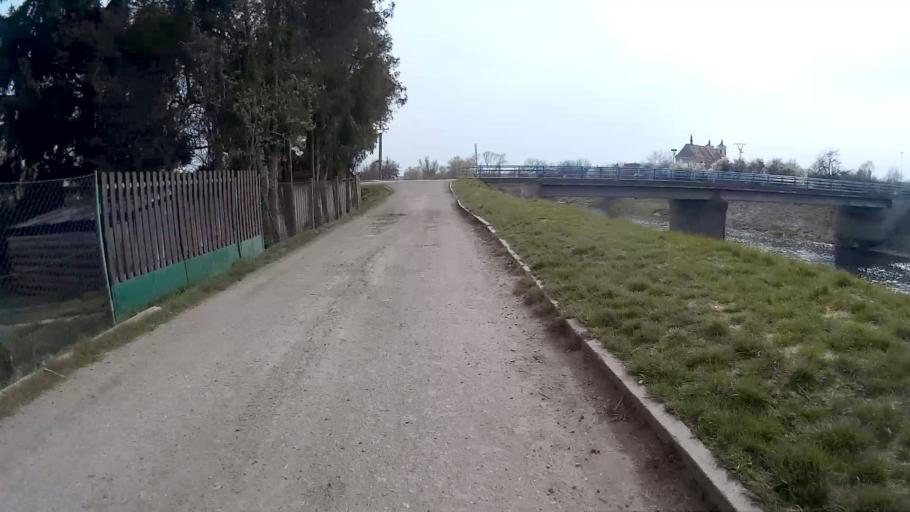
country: CZ
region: South Moravian
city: Rajhradice
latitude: 49.0932
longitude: 16.6200
